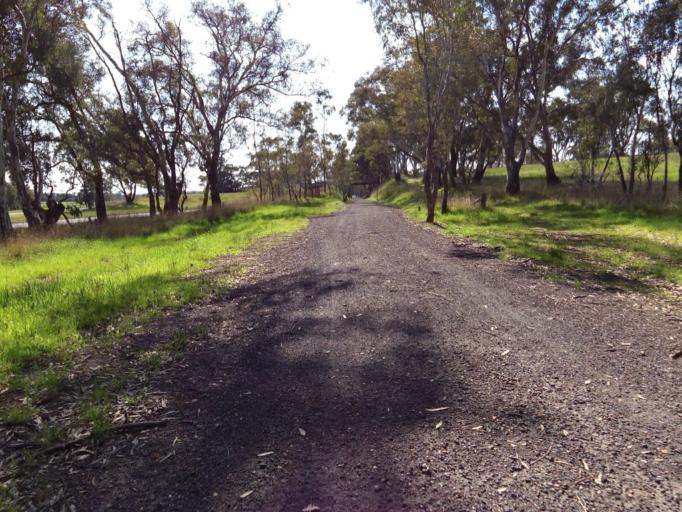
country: AU
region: Victoria
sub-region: Murrindindi
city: Alexandra
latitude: -37.1177
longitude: 145.6047
